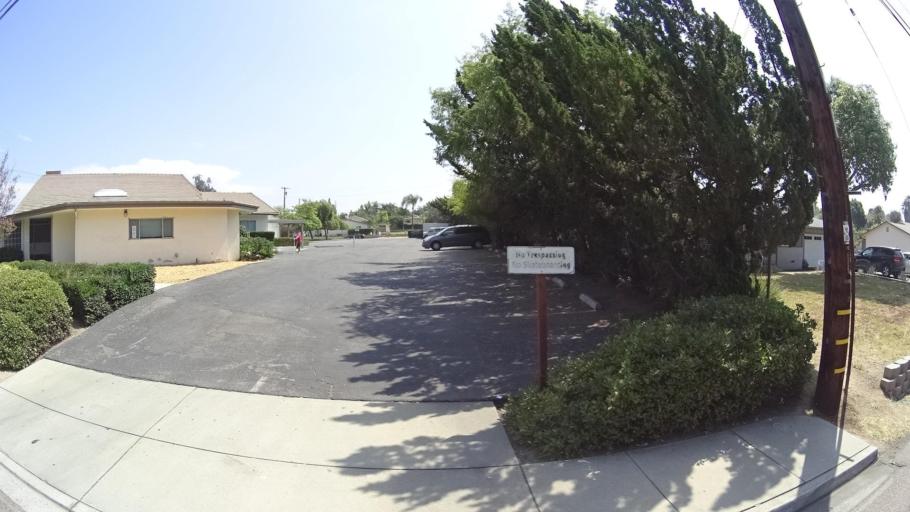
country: US
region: California
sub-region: San Diego County
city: Fallbrook
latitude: 33.3760
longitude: -117.2364
